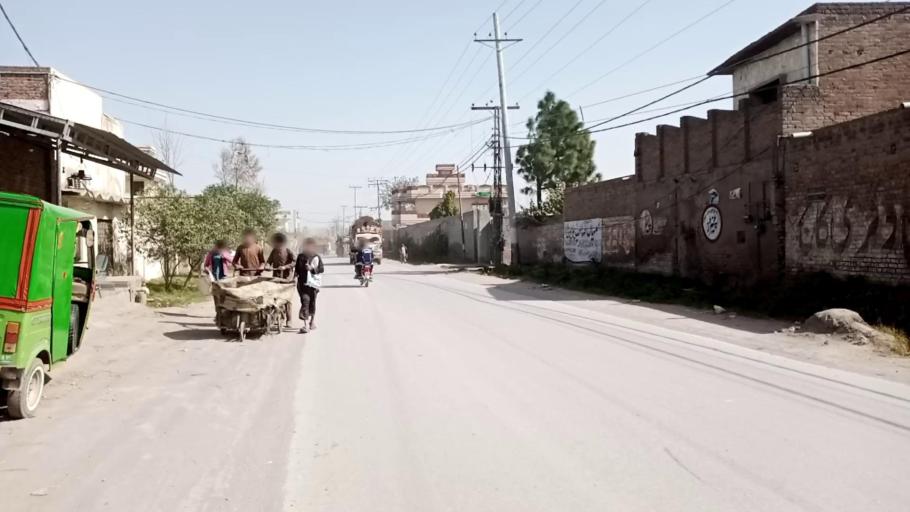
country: PK
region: Khyber Pakhtunkhwa
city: Peshawar
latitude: 34.0088
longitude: 71.6445
